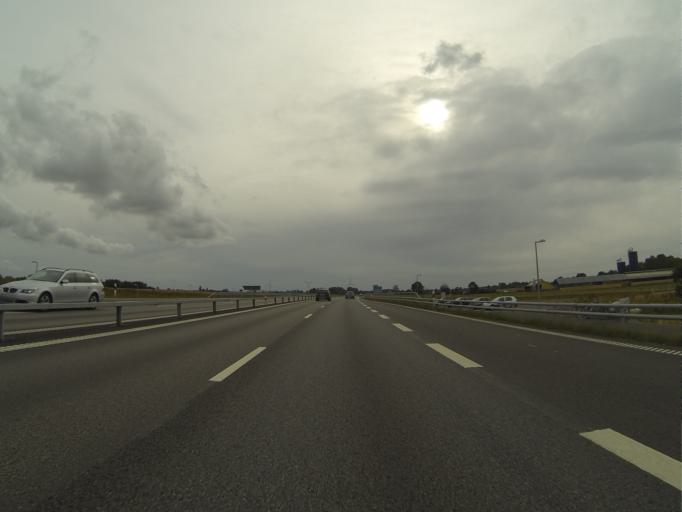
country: SE
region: Skane
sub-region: Hoors Kommun
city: Loberod
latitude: 55.8277
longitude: 13.5414
